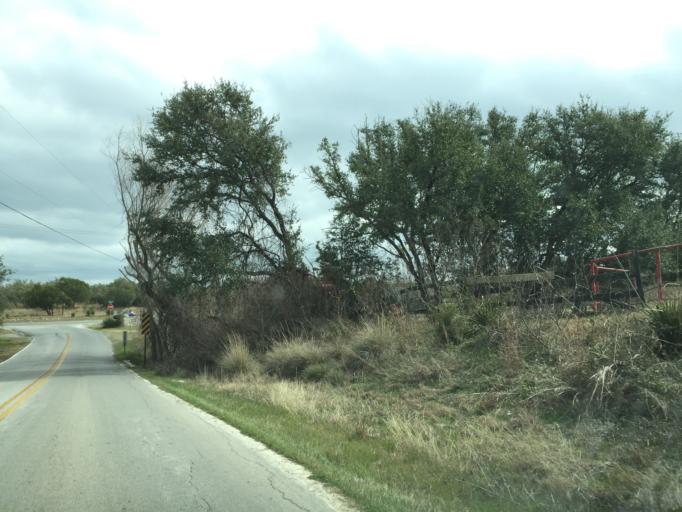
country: US
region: Texas
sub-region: Travis County
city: Briarcliff
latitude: 30.3768
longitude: -98.0819
